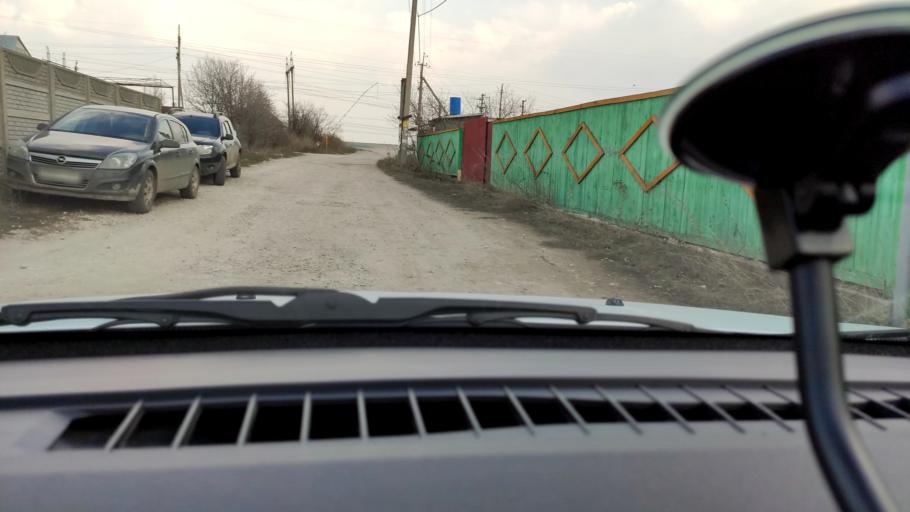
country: RU
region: Samara
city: Smyshlyayevka
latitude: 53.0910
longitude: 50.3955
